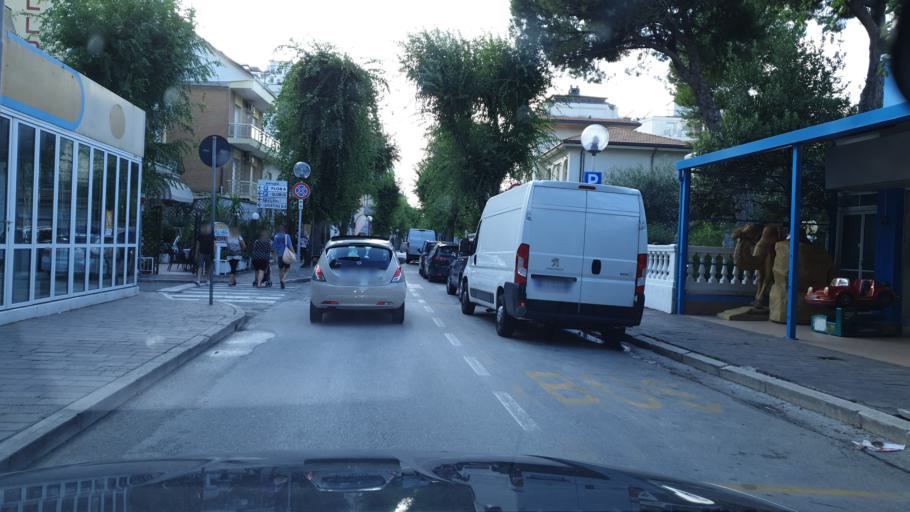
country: IT
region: Emilia-Romagna
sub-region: Provincia di Rimini
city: Cattolica
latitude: 43.9680
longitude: 12.7313
